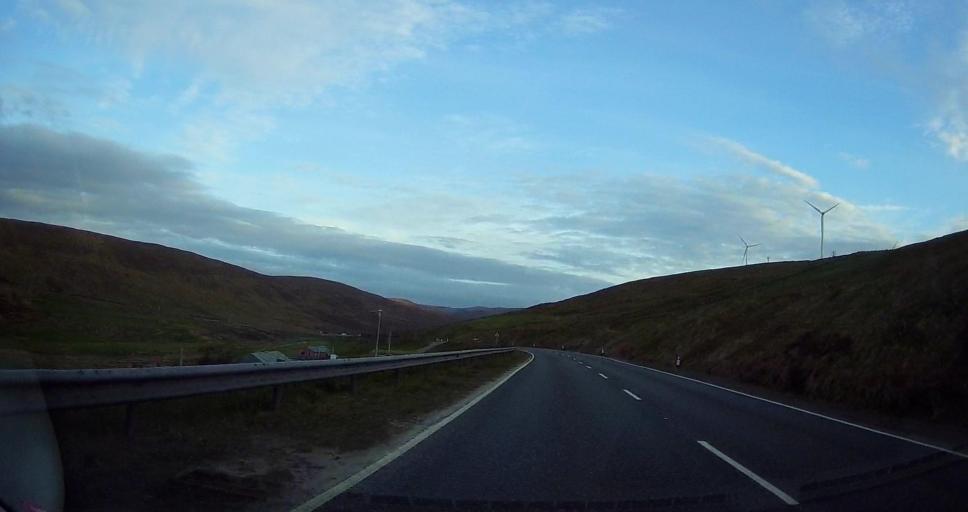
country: GB
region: Scotland
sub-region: Shetland Islands
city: Lerwick
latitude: 60.1686
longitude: -1.2265
